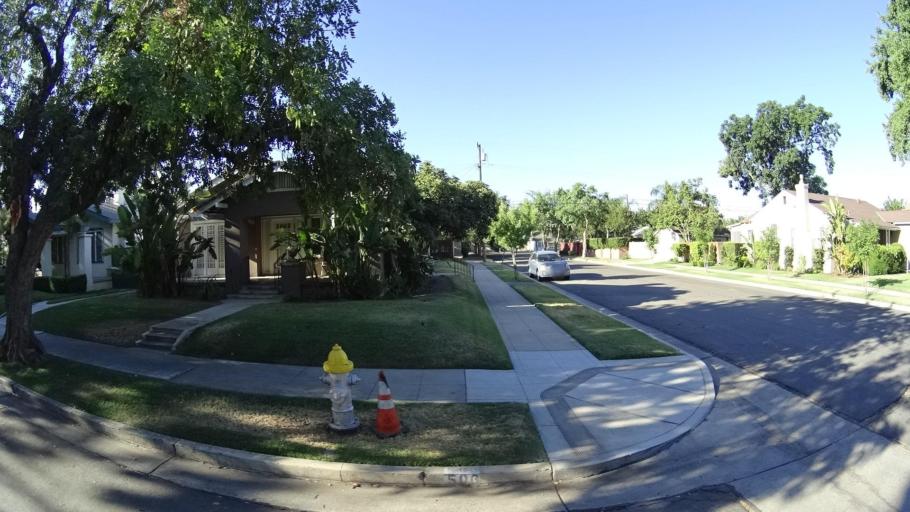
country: US
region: California
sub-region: Fresno County
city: Fresno
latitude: 36.7713
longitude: -119.8063
